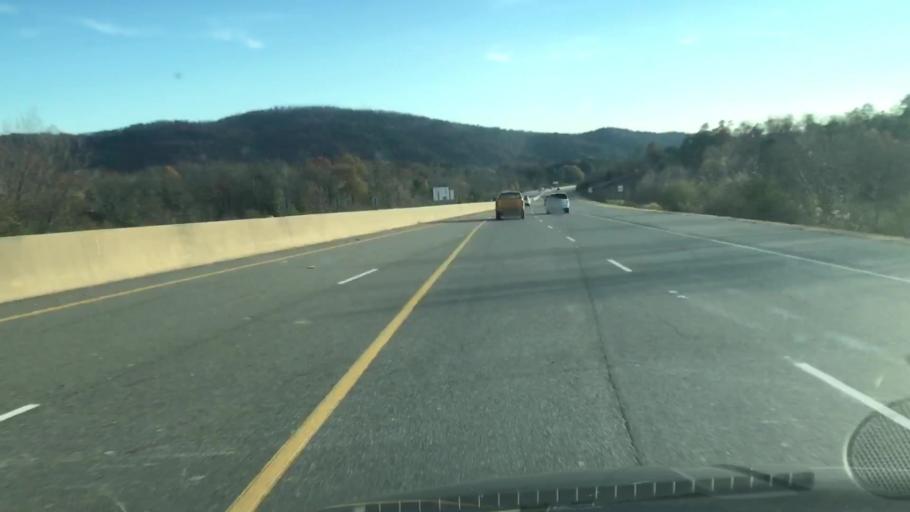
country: US
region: Arkansas
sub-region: Garland County
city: Hot Springs
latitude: 34.5004
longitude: -92.9755
